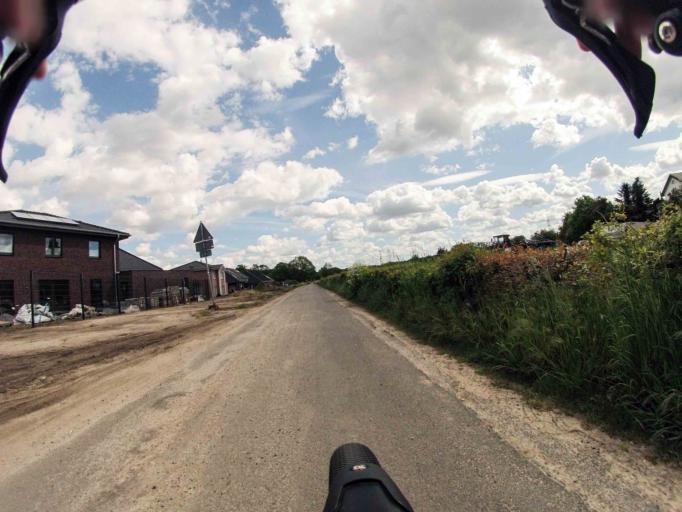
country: DE
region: North Rhine-Westphalia
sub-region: Regierungsbezirk Munster
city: Westerkappeln
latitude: 52.3171
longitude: 7.8892
